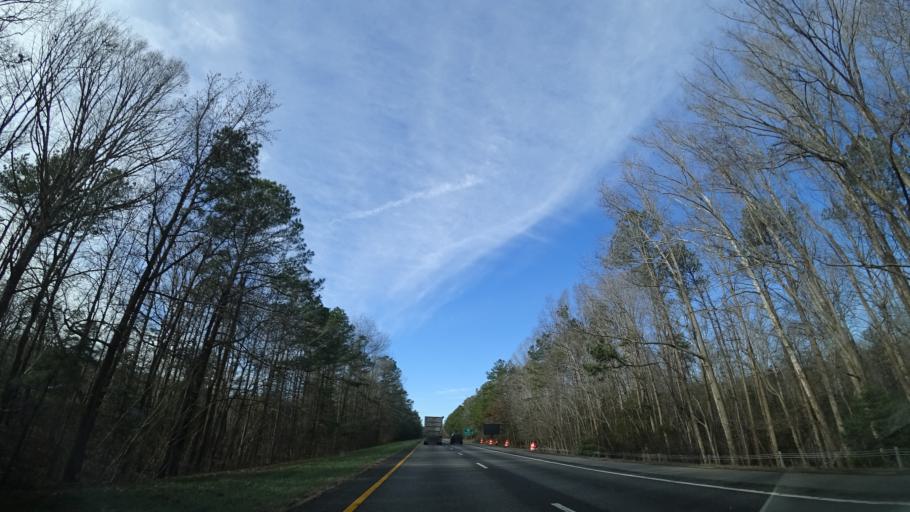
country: US
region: Virginia
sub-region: New Kent County
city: New Kent
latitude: 37.5016
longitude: -77.0753
